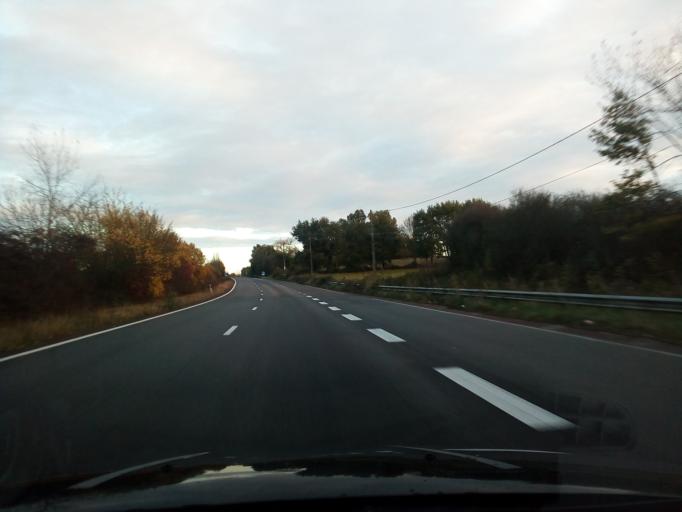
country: FR
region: Poitou-Charentes
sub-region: Departement de la Charente-Maritime
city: Chevanceaux
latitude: 45.3165
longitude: -0.2301
